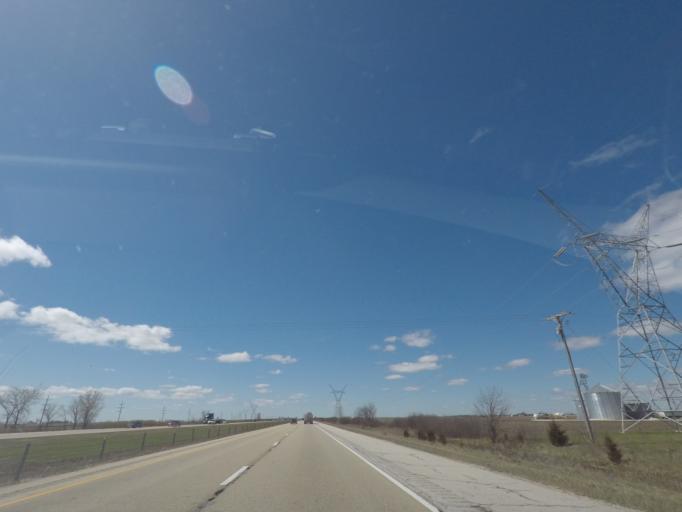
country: US
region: Illinois
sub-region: Livingston County
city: Dwight
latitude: 41.1403
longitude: -88.3694
